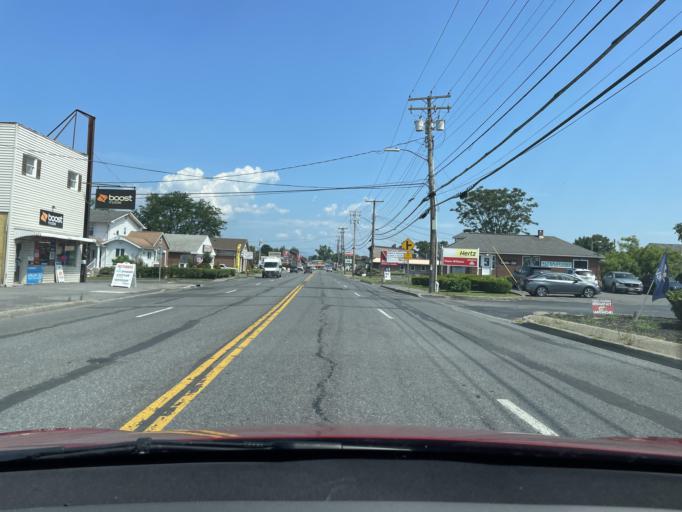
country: US
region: New York
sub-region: Ulster County
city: Lincoln Park
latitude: 41.9515
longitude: -73.9941
